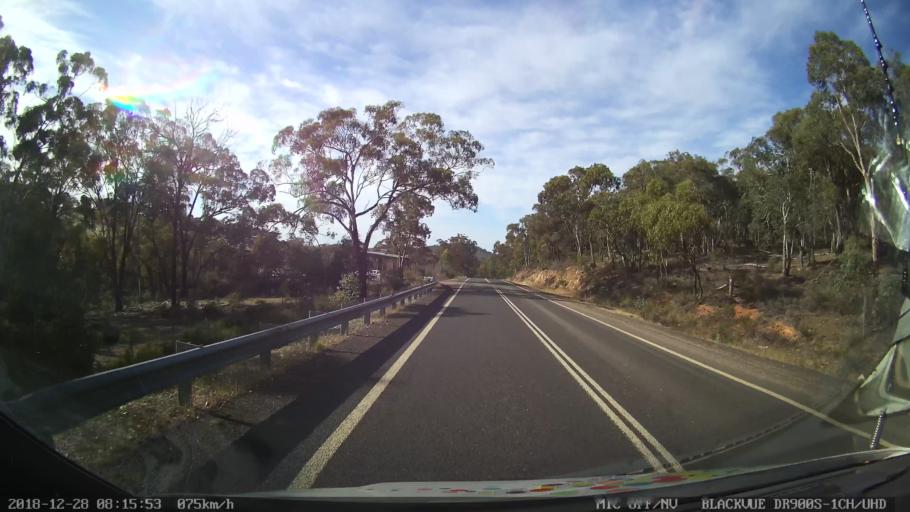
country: AU
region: New South Wales
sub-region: Blayney
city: Blayney
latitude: -33.8271
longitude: 149.3295
